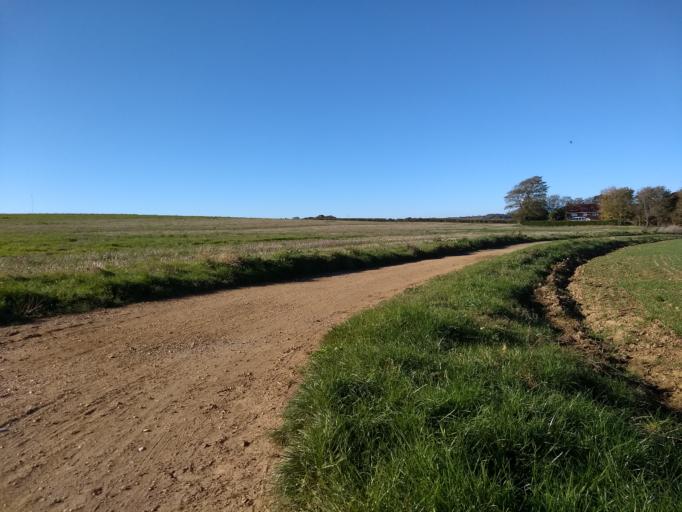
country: GB
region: England
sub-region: Isle of Wight
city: Newport
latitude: 50.6628
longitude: -1.2664
